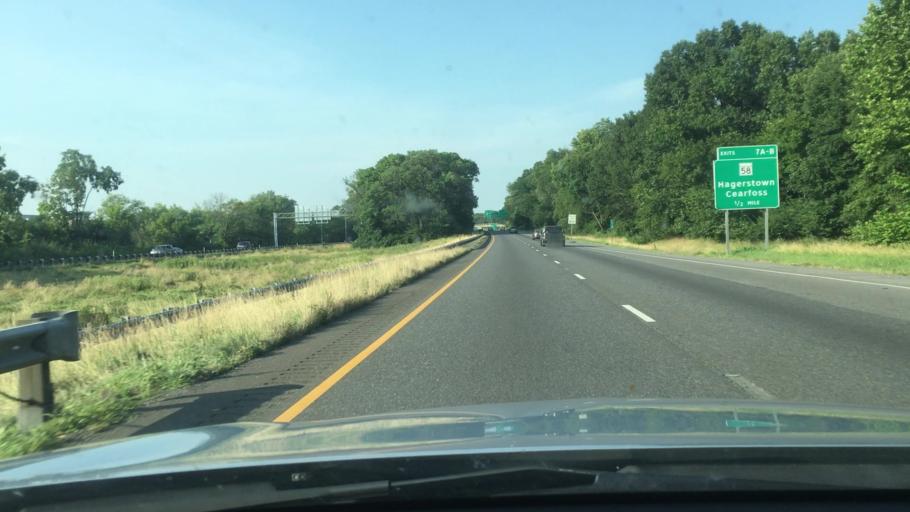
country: US
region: Maryland
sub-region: Washington County
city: Hagerstown
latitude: 39.6578
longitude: -77.7450
